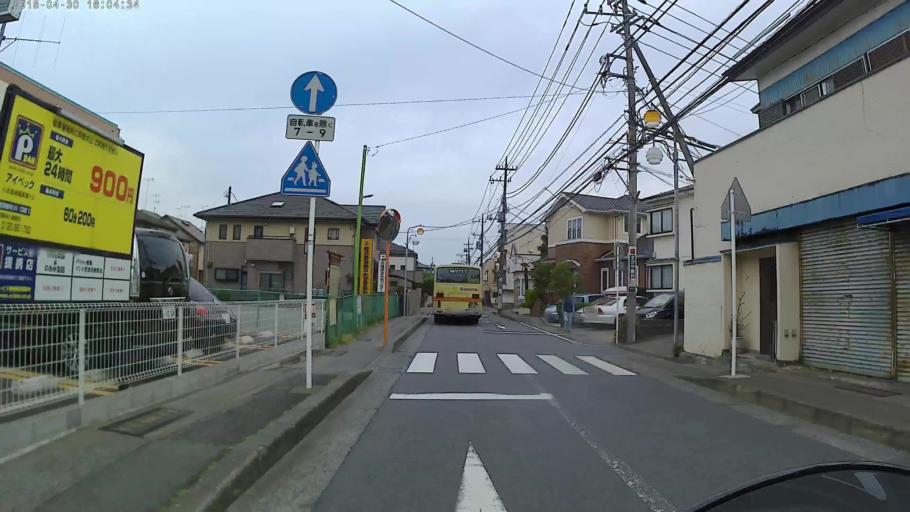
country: JP
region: Kanagawa
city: Minami-rinkan
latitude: 35.5089
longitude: 139.4244
